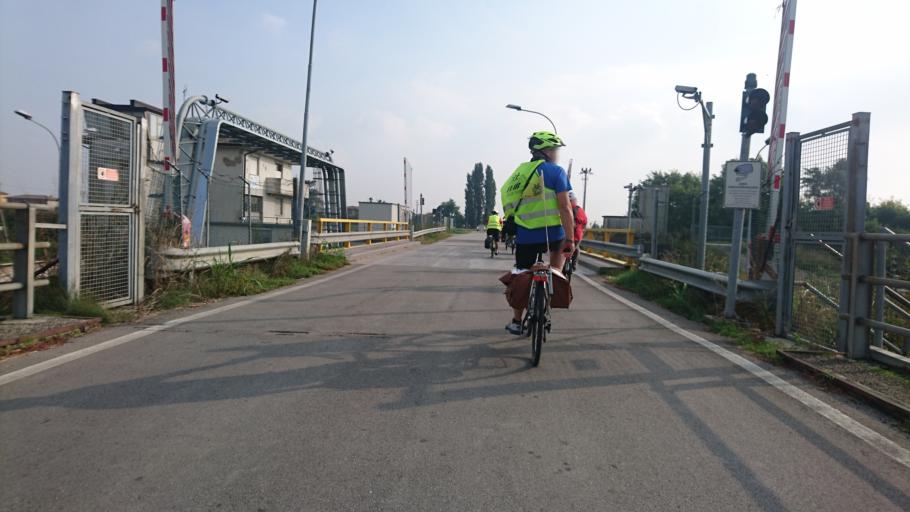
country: IT
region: Veneto
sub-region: Provincia di Rovigo
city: Arqua Polesine
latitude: 44.9965
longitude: 11.7280
